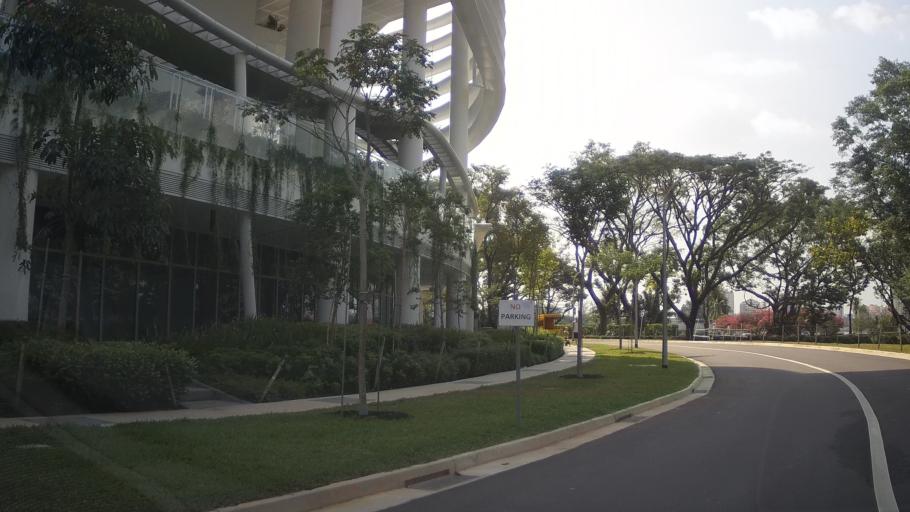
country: SG
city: Singapore
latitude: 1.3070
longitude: 103.8666
